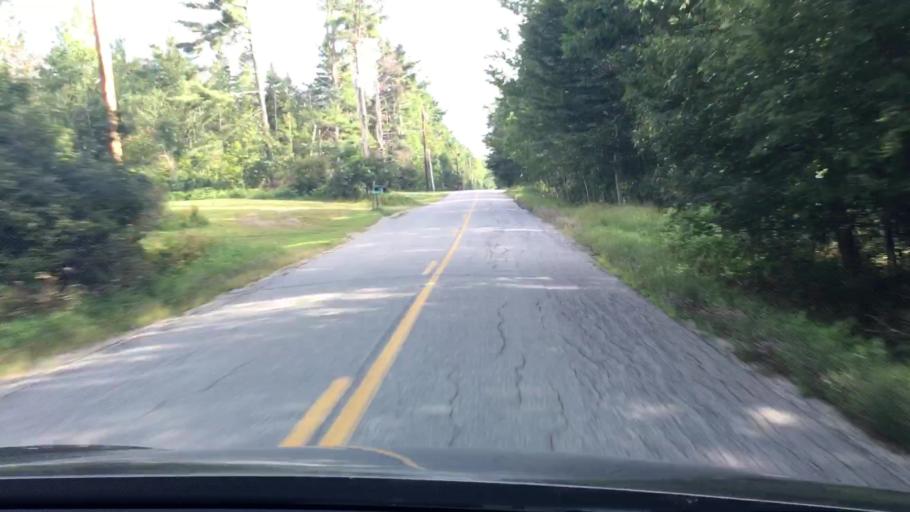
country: US
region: Maine
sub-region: Hancock County
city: Bucksport
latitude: 44.5373
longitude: -68.7943
